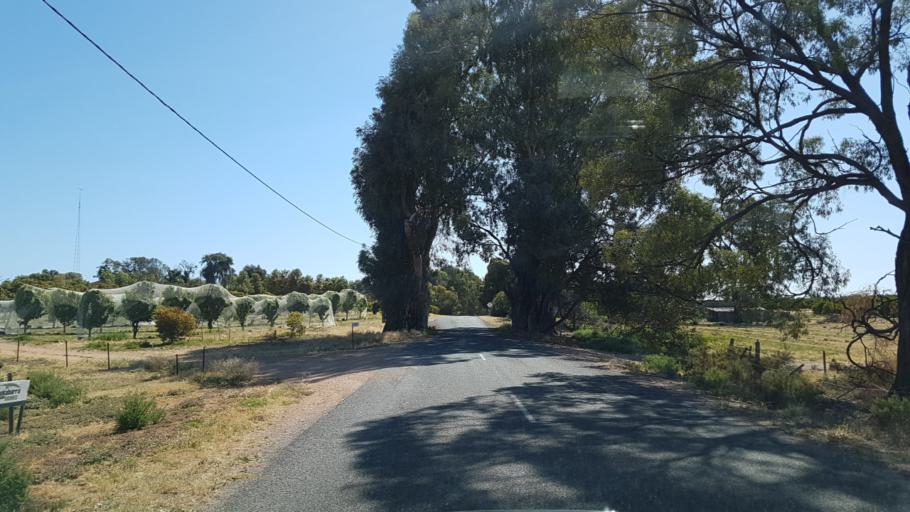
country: AU
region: South Australia
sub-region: Loxton Waikerie
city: Waikerie
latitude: -34.1661
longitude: 140.0281
